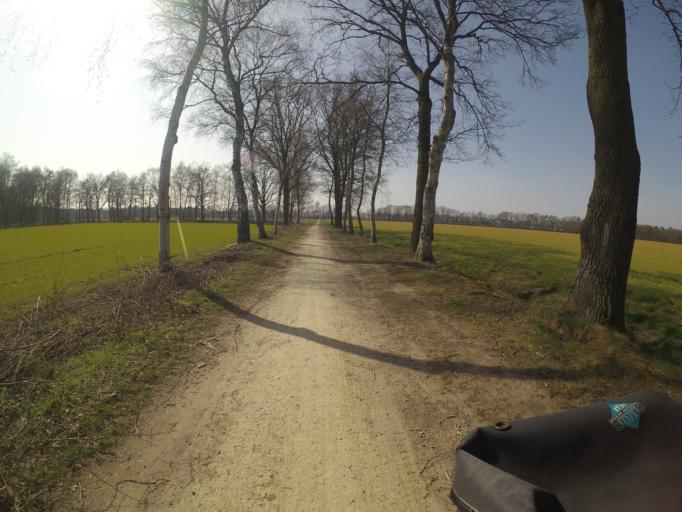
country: NL
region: North Brabant
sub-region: Gemeente Bernheze
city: Loosbroek
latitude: 51.6787
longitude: 5.4605
